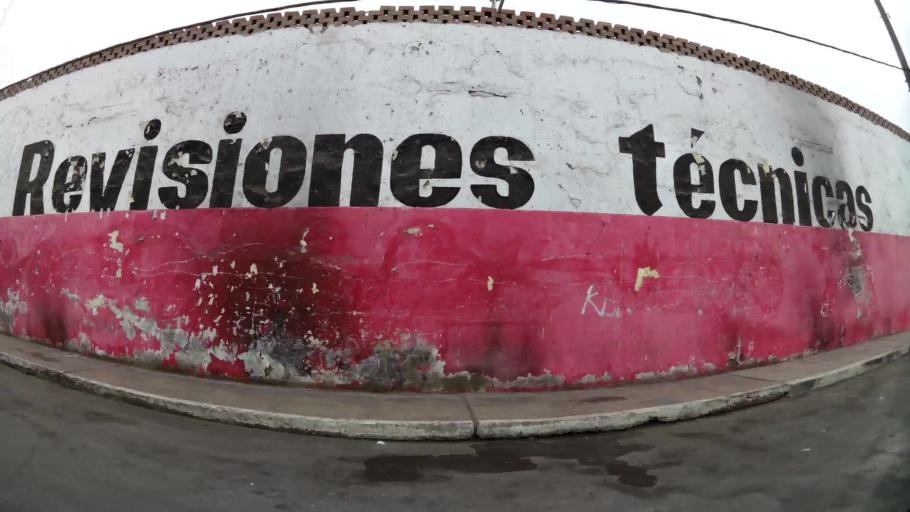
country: PE
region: Callao
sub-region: Callao
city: Callao
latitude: -12.0542
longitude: -77.1393
